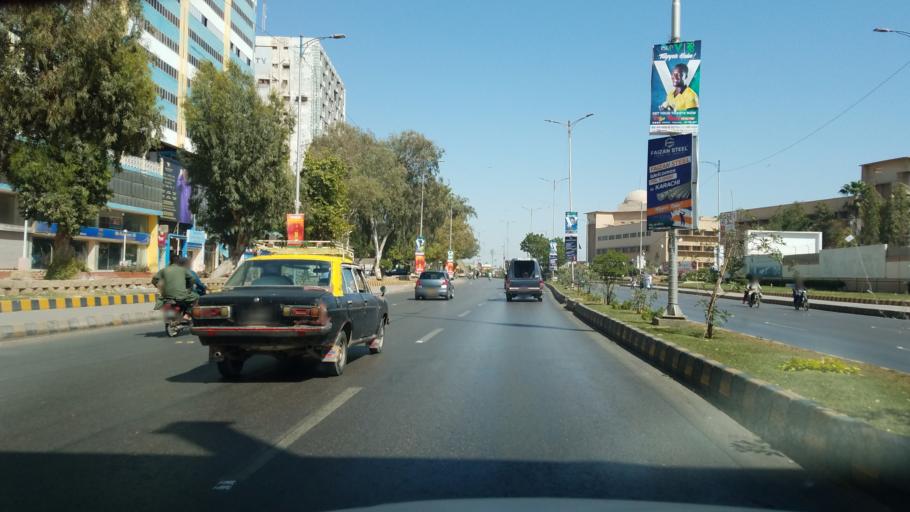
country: PK
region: Sindh
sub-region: Karachi District
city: Karachi
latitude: 24.8571
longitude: 67.0447
